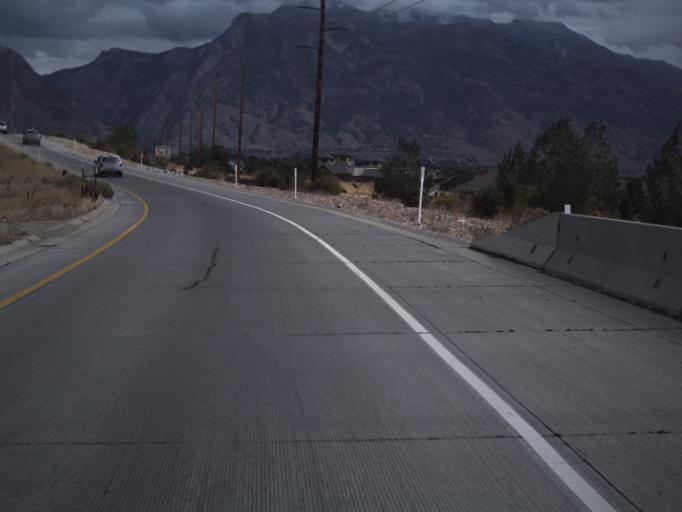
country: US
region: Utah
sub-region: Utah County
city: Lehi
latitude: 40.4315
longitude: -111.8412
